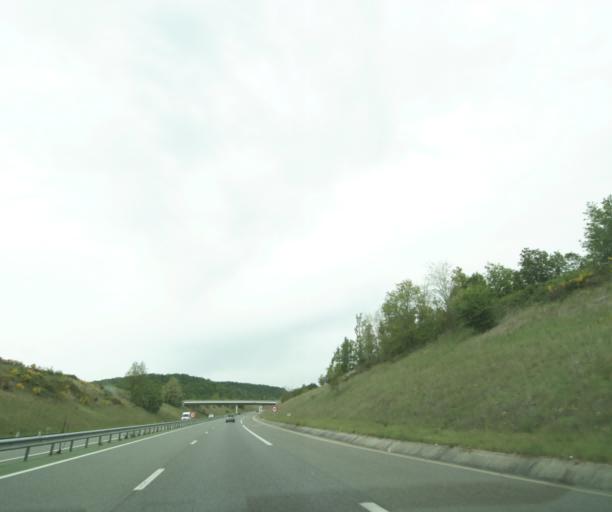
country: FR
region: Midi-Pyrenees
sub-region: Departement du Lot
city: Cahors
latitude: 44.4626
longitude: 1.5021
